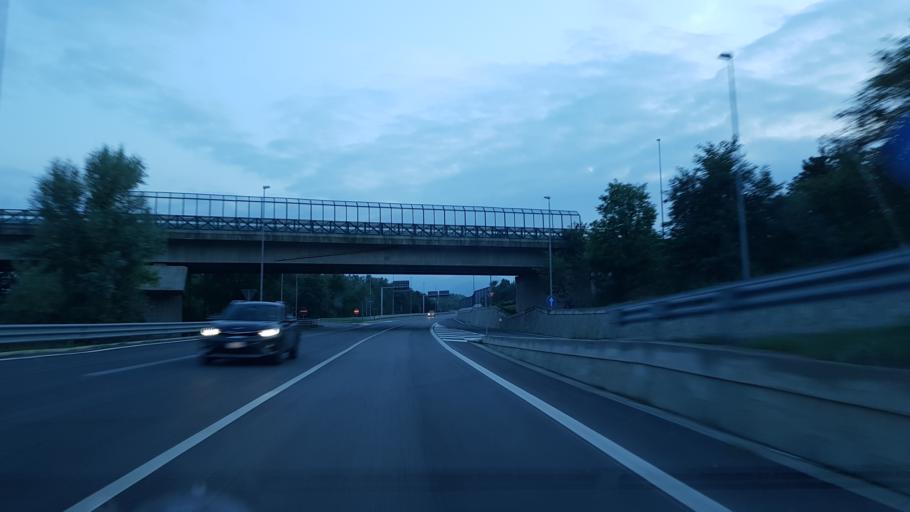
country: IT
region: Piedmont
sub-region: Provincia di Cuneo
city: Mondovi
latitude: 44.3910
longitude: 7.7961
